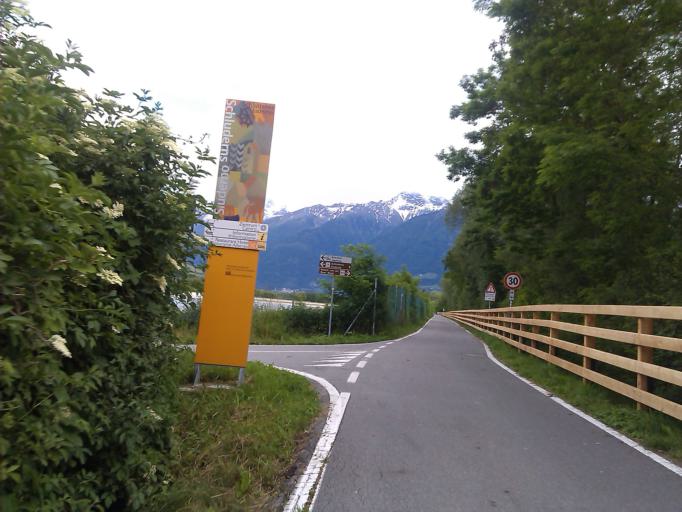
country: IT
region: Trentino-Alto Adige
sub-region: Bolzano
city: Glorenza
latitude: 46.6629
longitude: 10.5635
